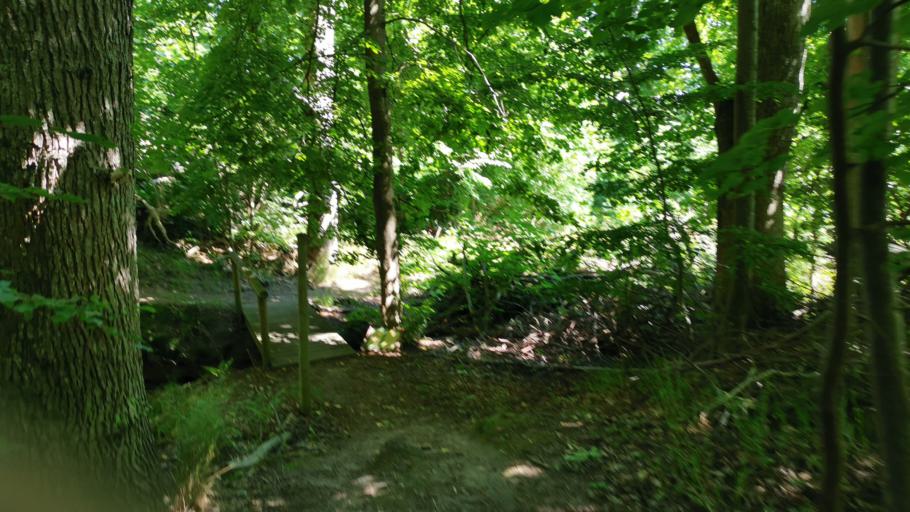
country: SE
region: Vaestra Goetaland
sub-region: Lysekils Kommun
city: Lysekil
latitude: 58.2408
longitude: 11.4886
